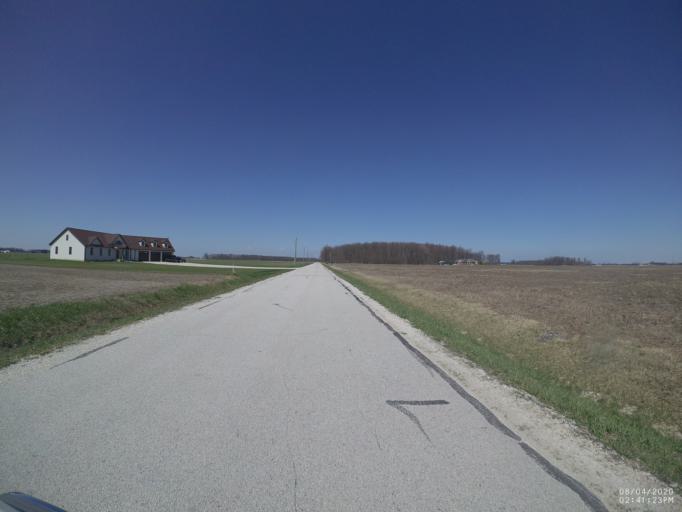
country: US
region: Ohio
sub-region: Sandusky County
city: Gibsonburg
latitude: 41.2858
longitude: -83.2969
